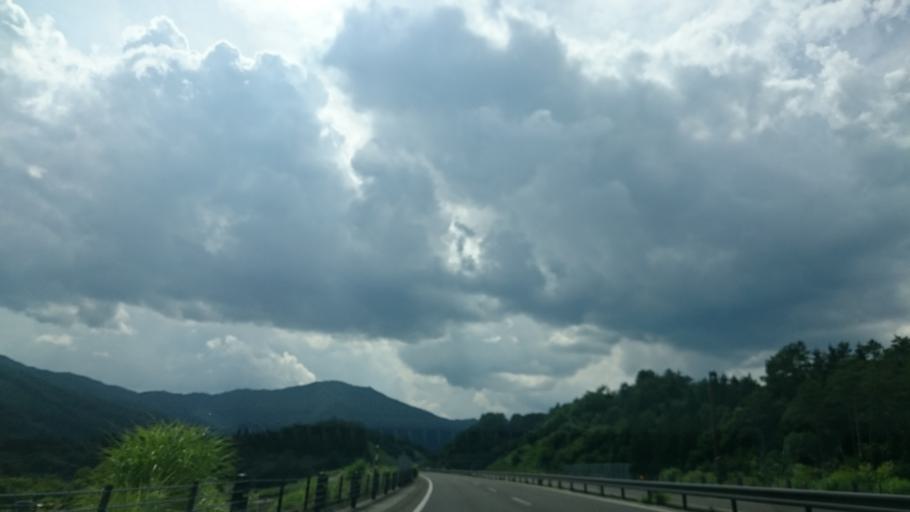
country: JP
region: Gifu
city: Takayama
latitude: 36.1391
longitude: 137.1721
